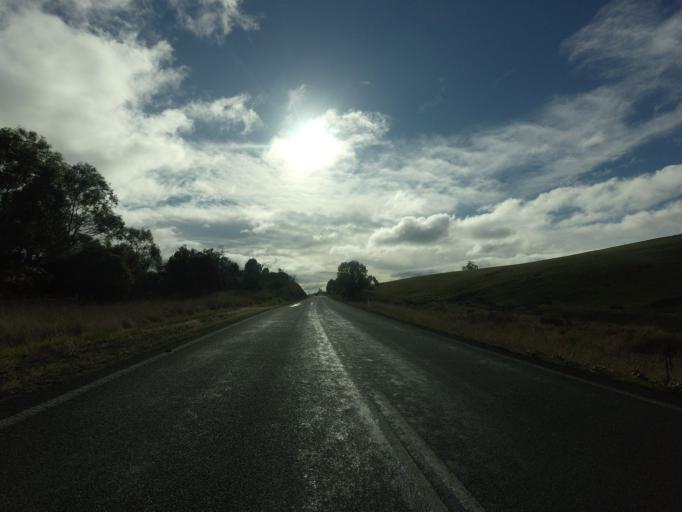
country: AU
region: Tasmania
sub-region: Derwent Valley
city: New Norfolk
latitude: -42.6070
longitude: 146.8848
